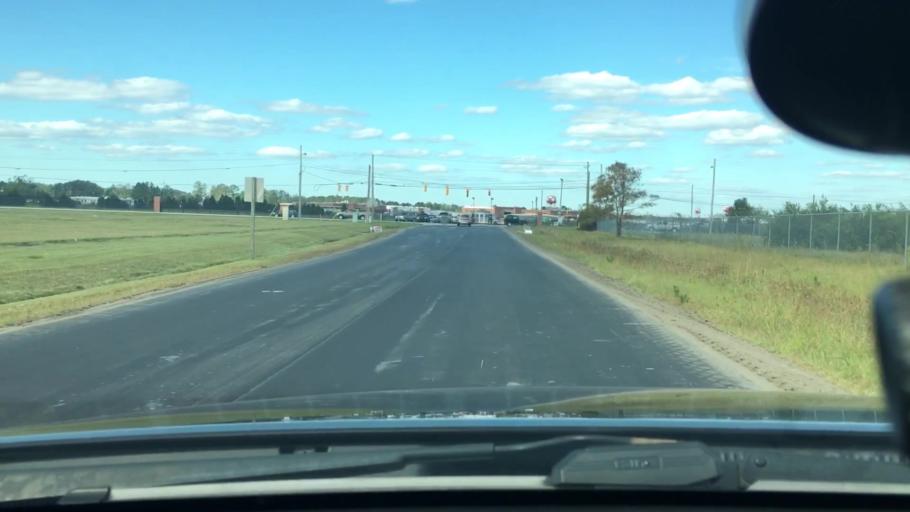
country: US
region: North Carolina
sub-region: Craven County
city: Havelock
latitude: 34.8812
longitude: -76.9007
